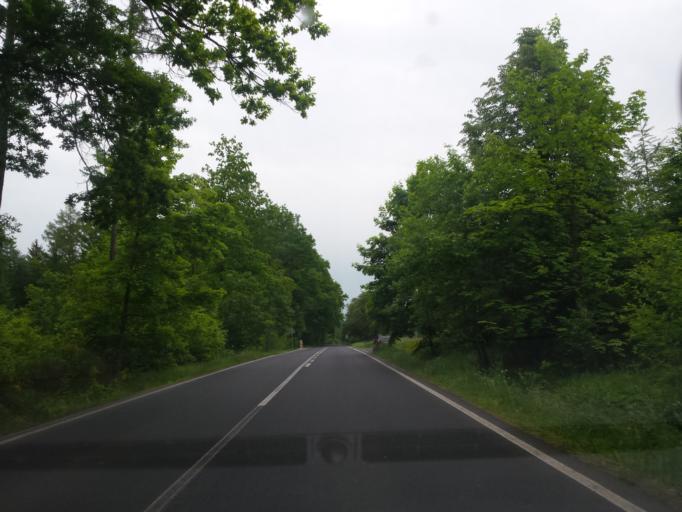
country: CZ
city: Novy Bor
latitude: 50.7487
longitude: 14.5716
